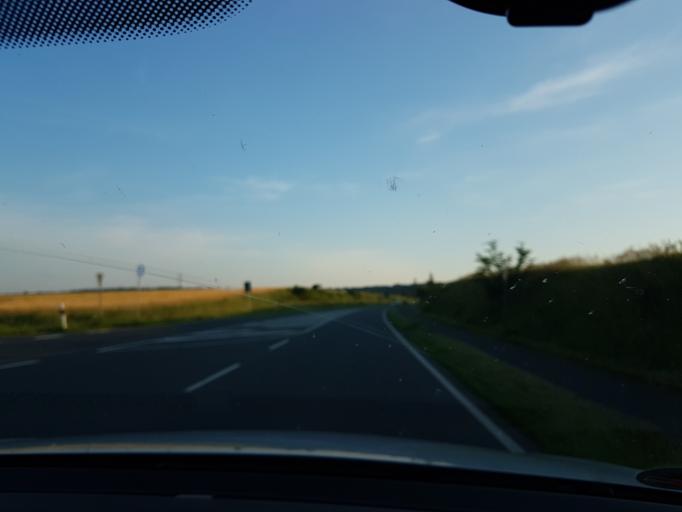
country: DE
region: Lower Saxony
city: Wolsdorf
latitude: 52.1955
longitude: 10.9683
